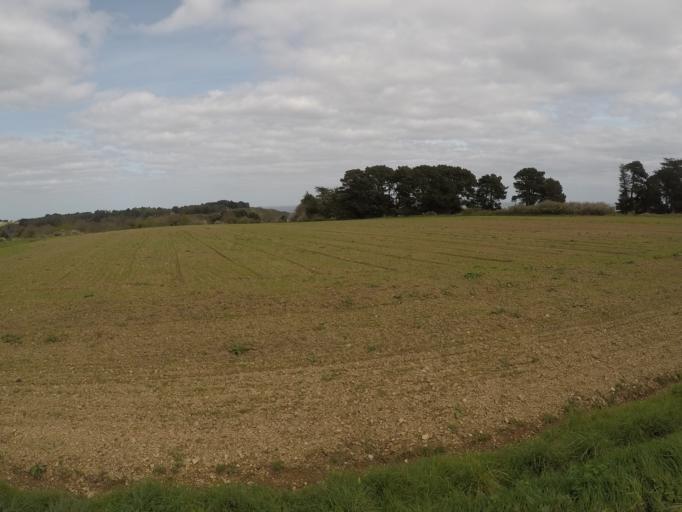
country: FR
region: Brittany
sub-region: Departement des Cotes-d'Armor
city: Plouezec
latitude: 48.7232
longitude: -2.9545
